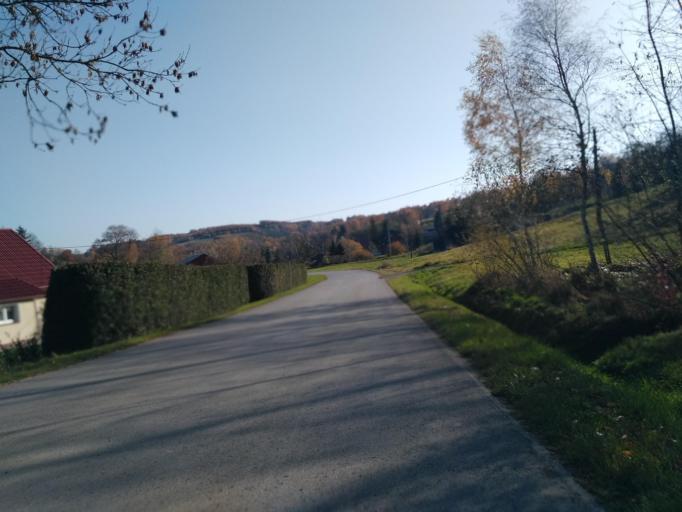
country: PL
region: Subcarpathian Voivodeship
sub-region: Powiat brzozowski
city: Nozdrzec
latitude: 49.7963
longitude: 22.1759
